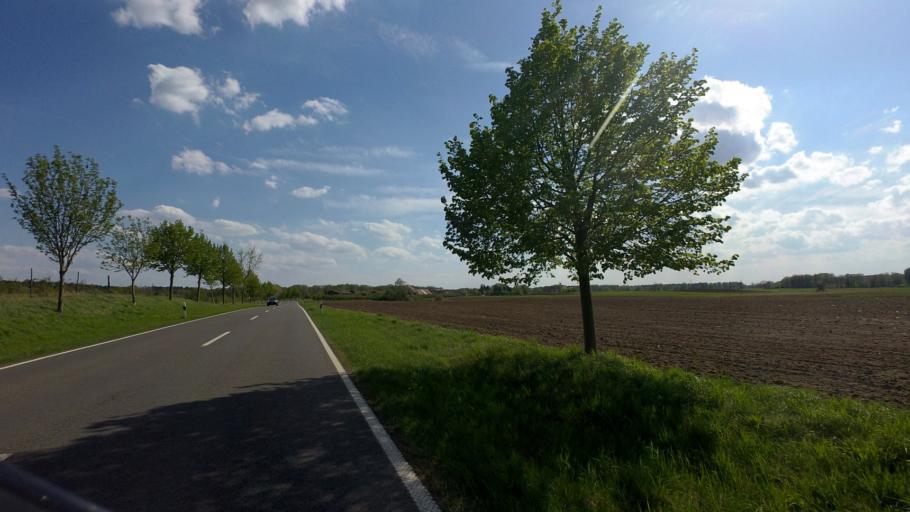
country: DE
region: Brandenburg
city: Templin
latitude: 53.0955
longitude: 13.5010
